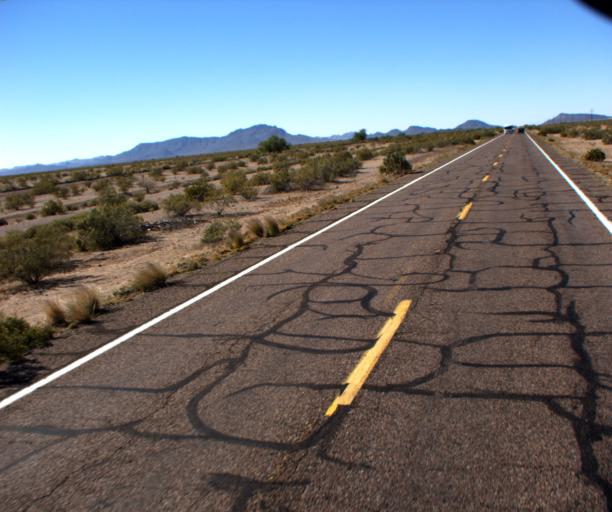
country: US
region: Arizona
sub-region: Maricopa County
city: Gila Bend
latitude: 32.8545
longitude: -112.7690
